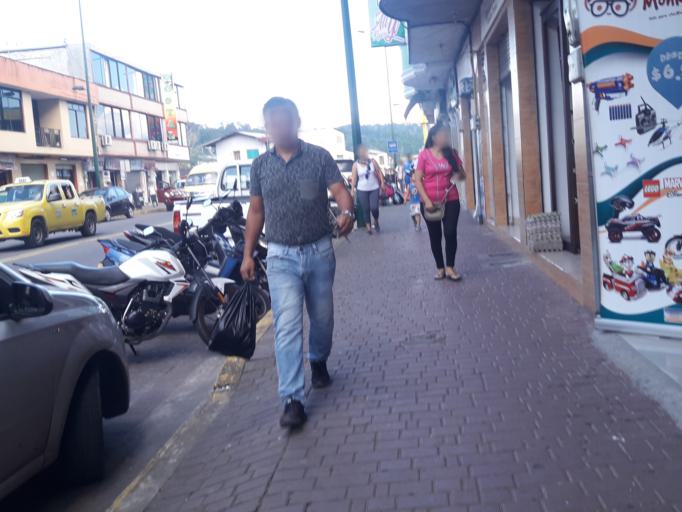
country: EC
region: Napo
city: Tena
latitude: -0.9942
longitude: -77.8137
